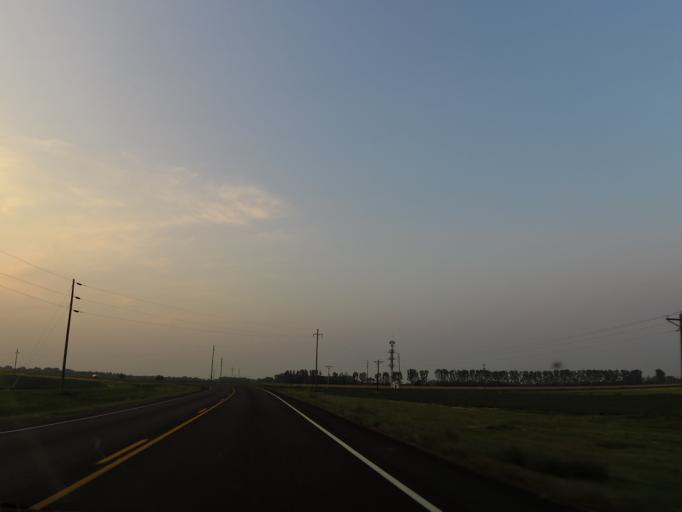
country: US
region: North Dakota
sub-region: Walsh County
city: Park River
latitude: 48.3960
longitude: -97.6229
